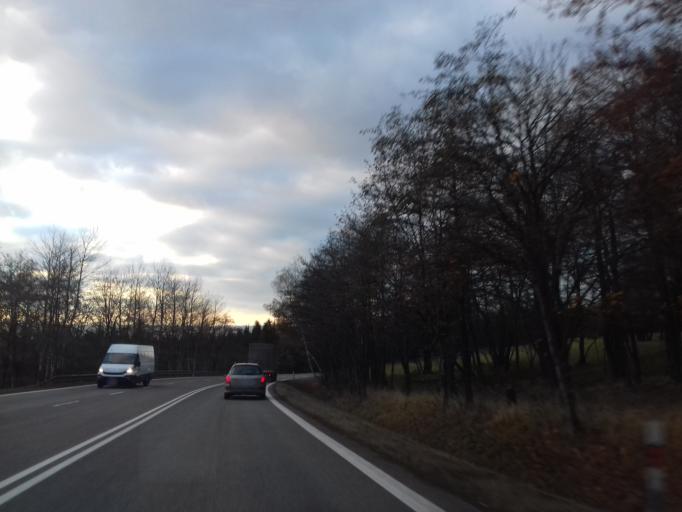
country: CZ
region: Pardubicky
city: Prosec
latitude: 49.7645
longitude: 16.0948
